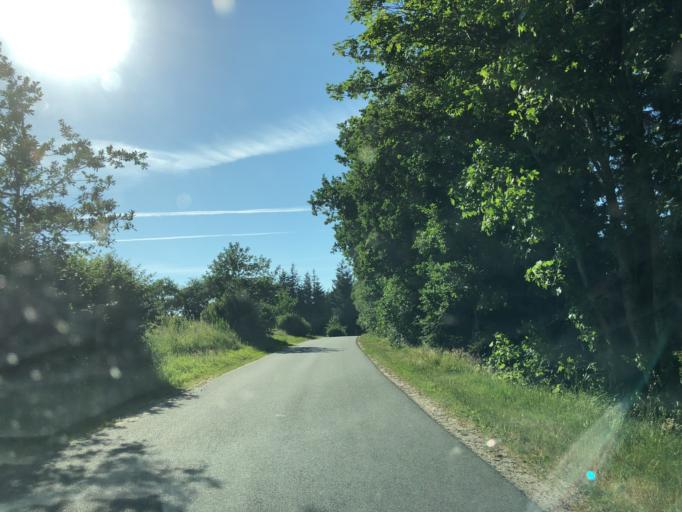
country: DK
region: Central Jutland
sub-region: Holstebro Kommune
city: Ulfborg
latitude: 56.3200
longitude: 8.3765
